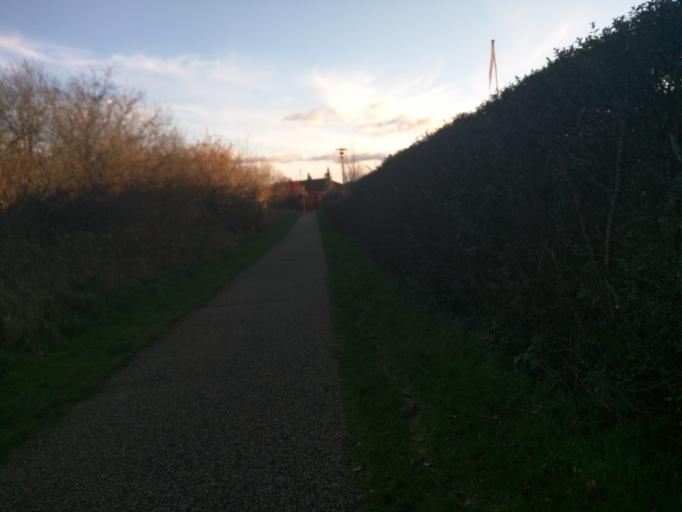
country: DK
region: Central Jutland
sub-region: Skanderborg Kommune
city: Horning
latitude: 56.0872
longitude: 10.0218
